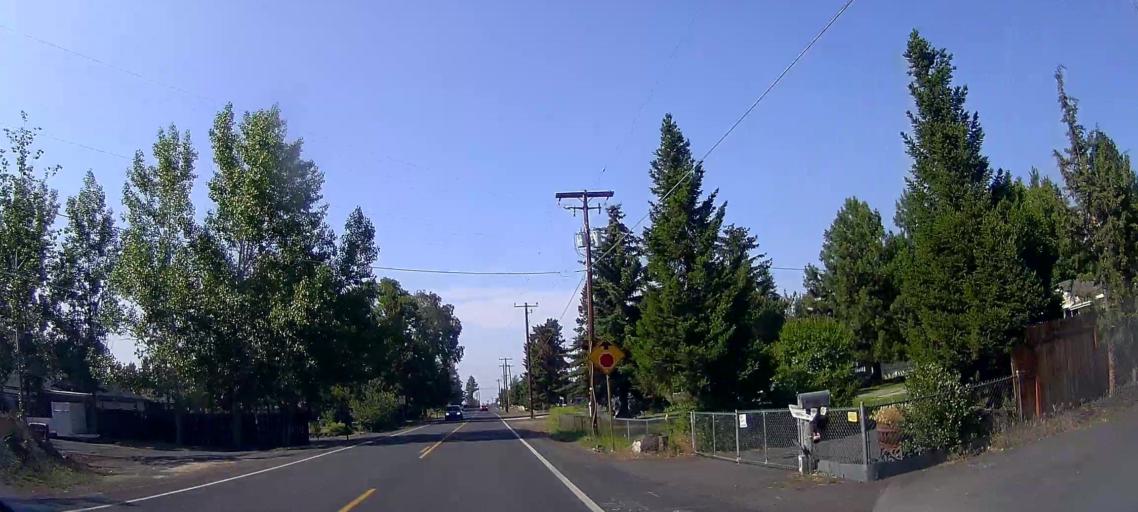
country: US
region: Oregon
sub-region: Deschutes County
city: Bend
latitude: 44.0497
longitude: -121.2686
